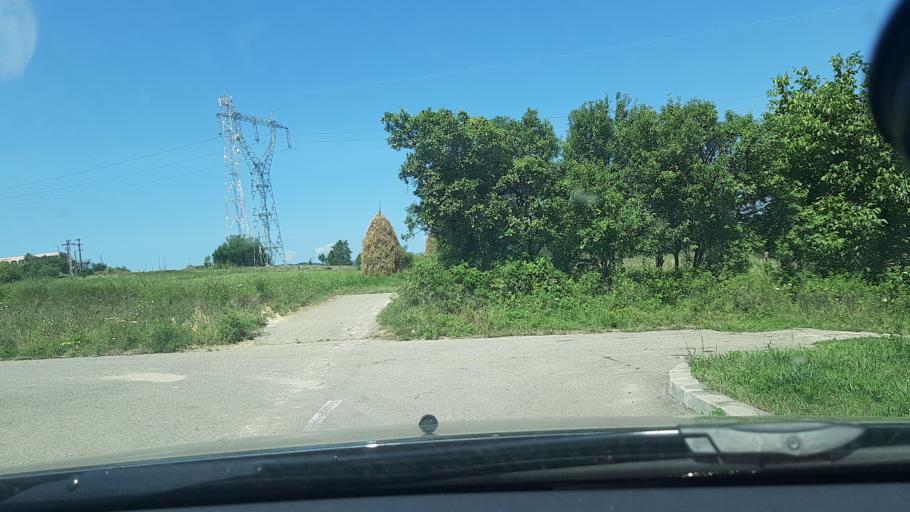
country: RO
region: Hunedoara
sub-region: Comuna Teliucu Inferior
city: Teliucu Inferior
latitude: 45.7041
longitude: 22.8883
